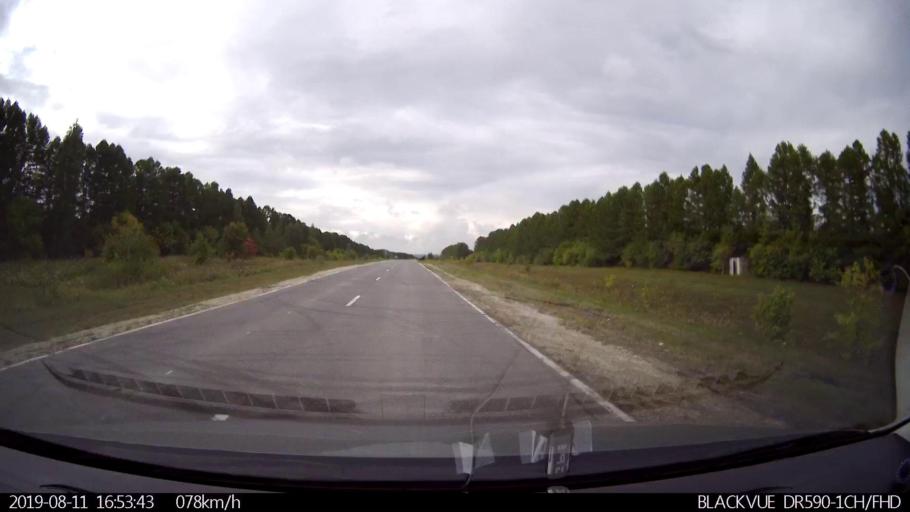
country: RU
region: Ulyanovsk
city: Mayna
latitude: 54.2656
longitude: 47.6692
